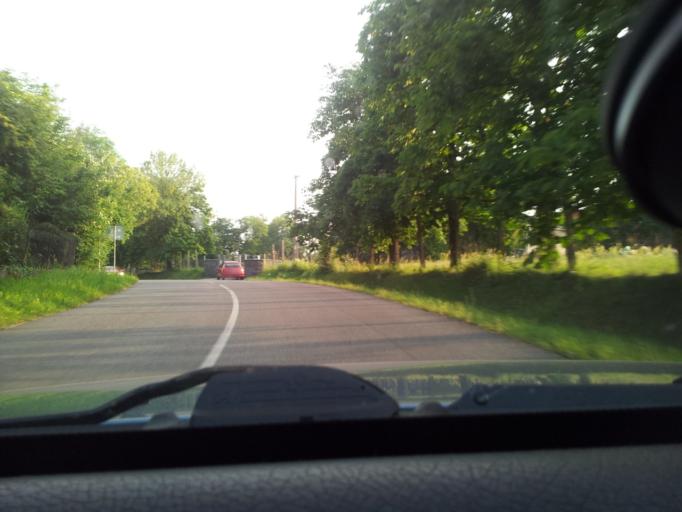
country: SK
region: Banskobystricky
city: Nova Bana
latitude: 48.3480
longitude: 18.7235
